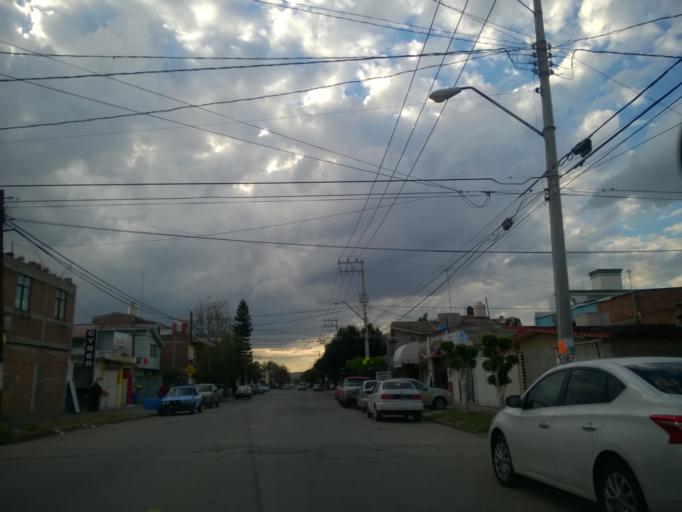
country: MX
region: Guanajuato
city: Leon
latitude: 21.1063
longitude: -101.6487
